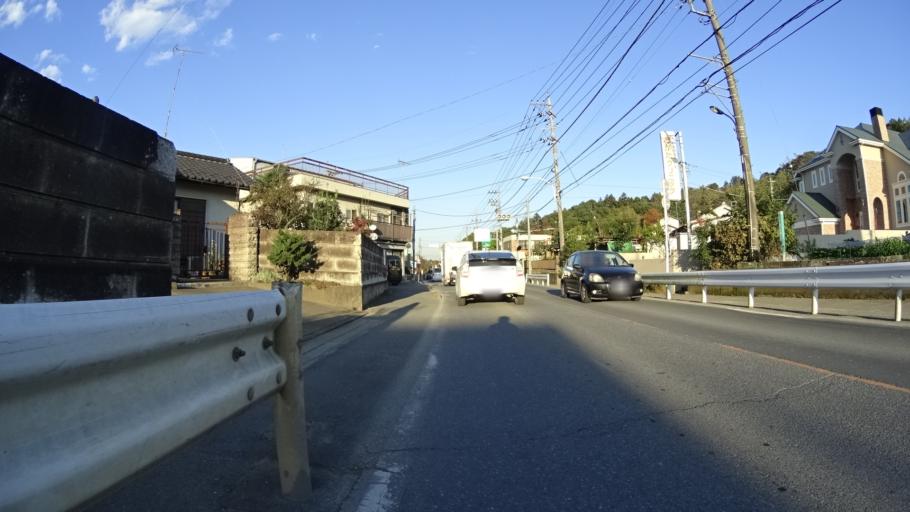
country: JP
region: Tokyo
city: Hachioji
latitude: 35.6799
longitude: 139.2725
